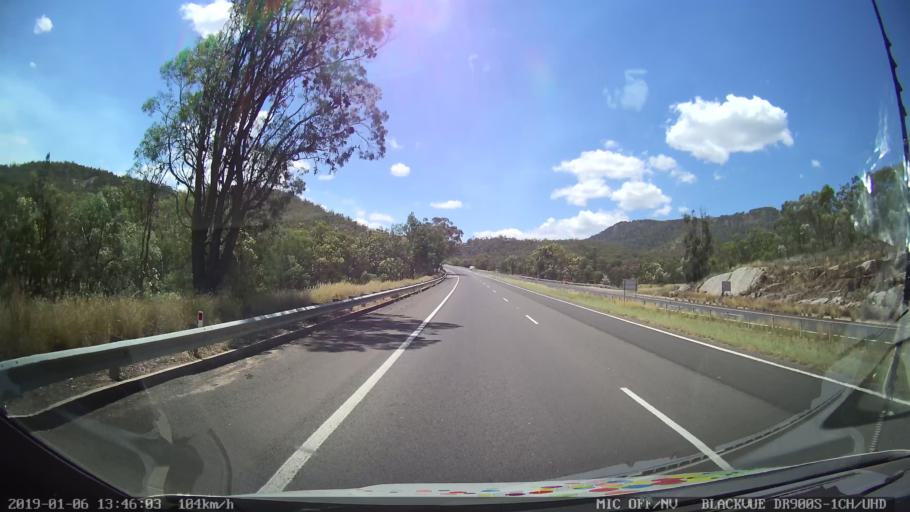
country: AU
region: New South Wales
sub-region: Tamworth Municipality
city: Kootingal
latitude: -30.9831
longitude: 151.0991
